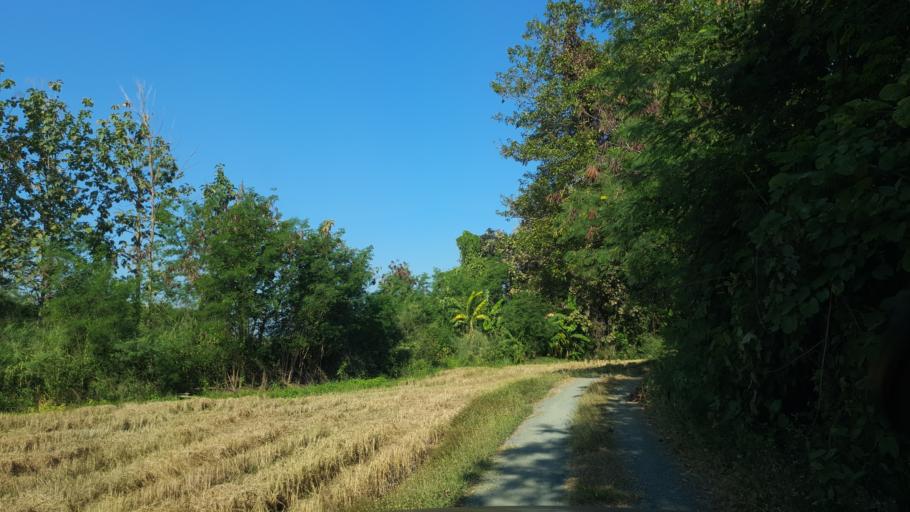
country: TH
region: Chiang Mai
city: San Kamphaeng
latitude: 18.7333
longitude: 99.1711
